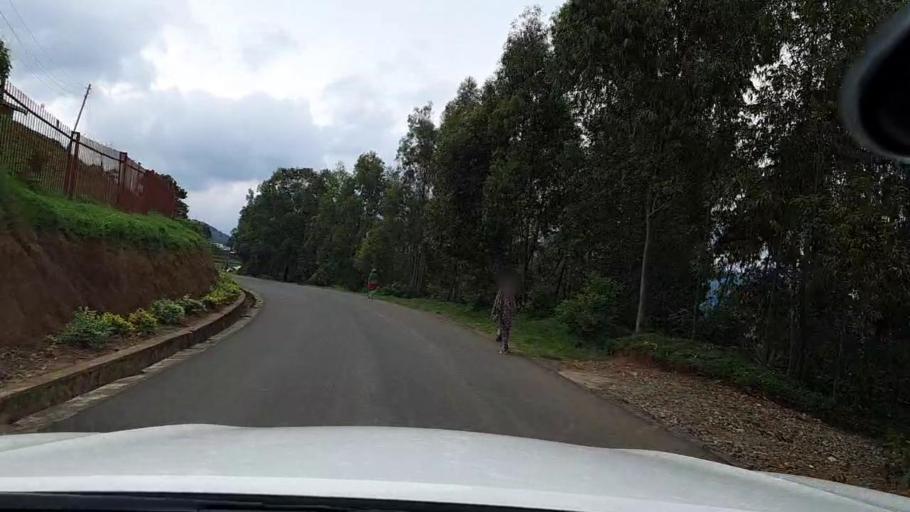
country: RW
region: Western Province
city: Kibuye
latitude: -2.1809
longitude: 29.2917
